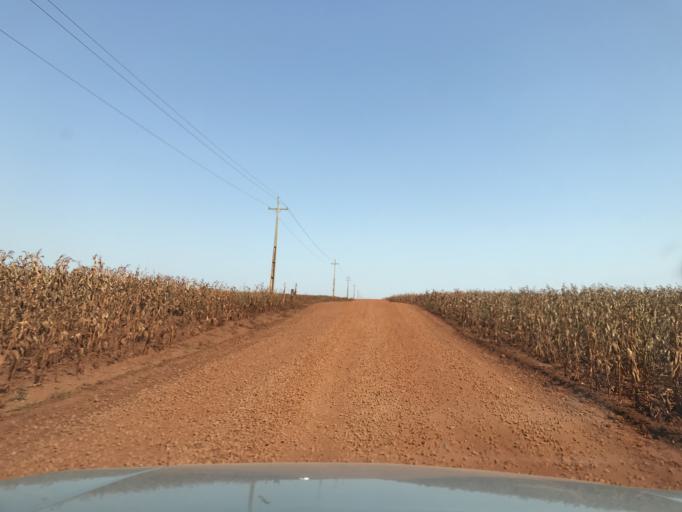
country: BR
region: Parana
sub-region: Palotina
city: Palotina
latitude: -24.2531
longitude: -53.7349
